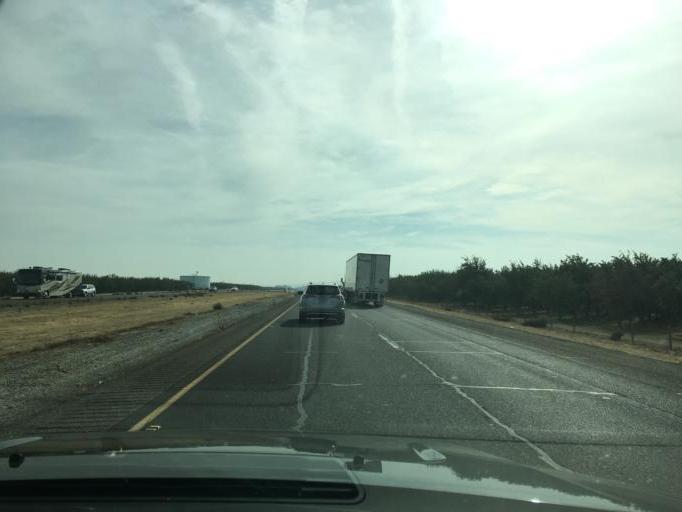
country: US
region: California
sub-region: Fresno County
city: Huron
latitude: 36.1072
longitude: -120.1311
